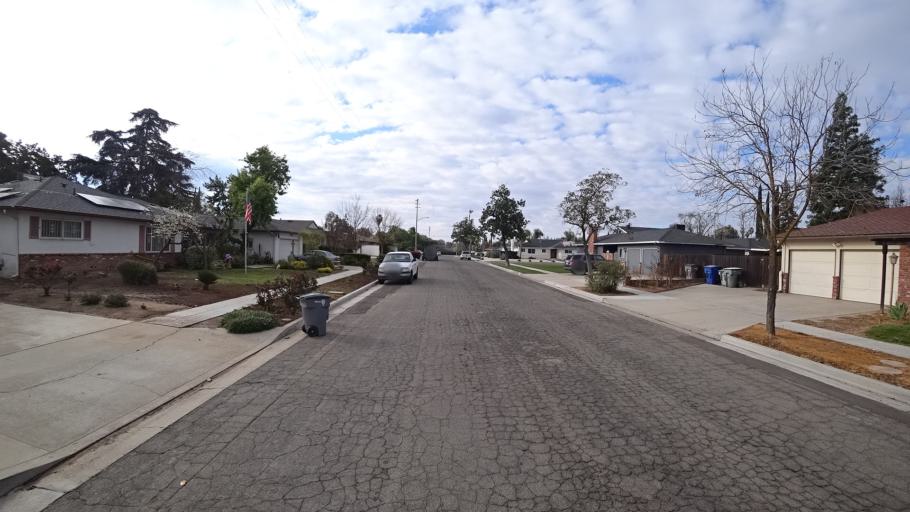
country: US
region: California
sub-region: Fresno County
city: Clovis
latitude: 36.8249
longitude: -119.7591
